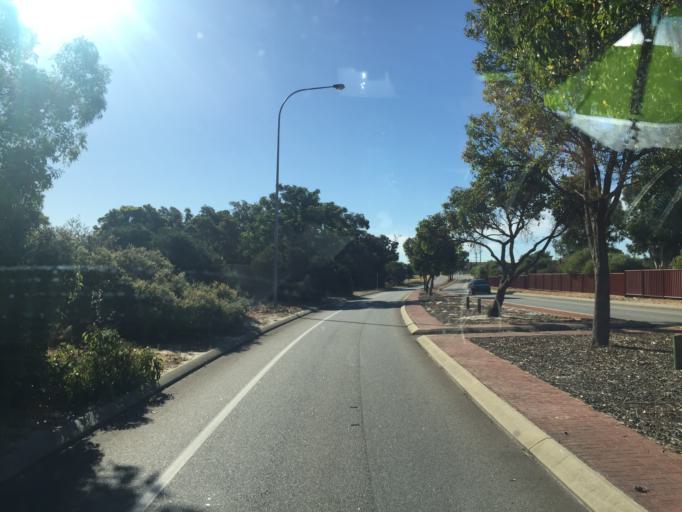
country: AU
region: Western Australia
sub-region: Canning
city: East Cannington
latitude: -32.0031
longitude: 115.9713
